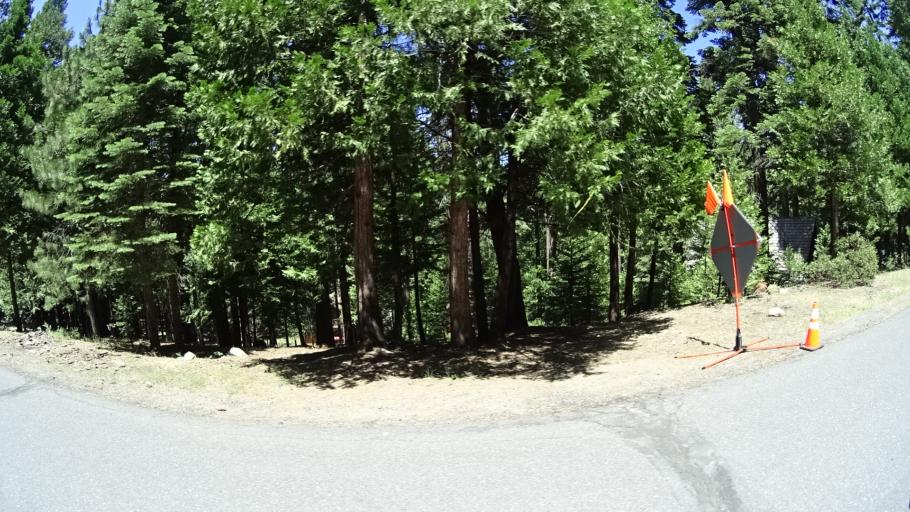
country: US
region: California
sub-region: Calaveras County
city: Arnold
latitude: 38.3165
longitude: -120.2552
